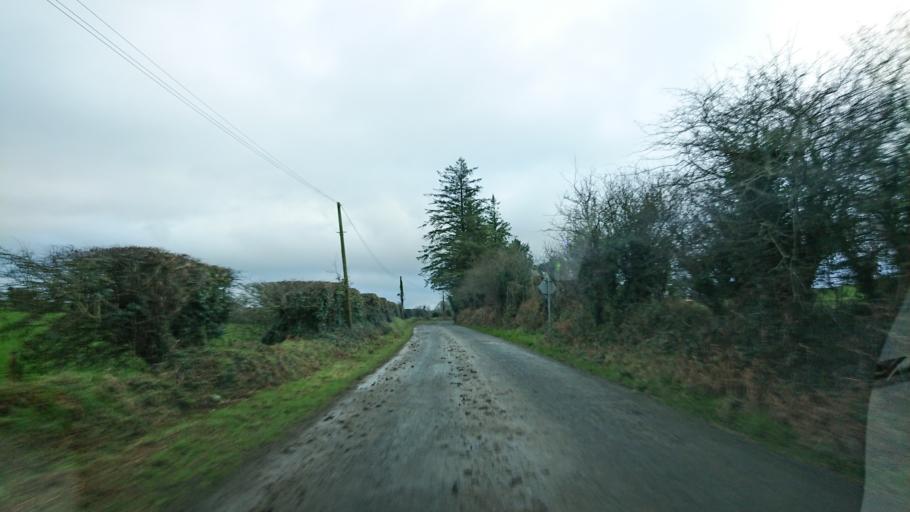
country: IE
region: Munster
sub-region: Waterford
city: Portlaw
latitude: 52.2552
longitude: -7.4067
